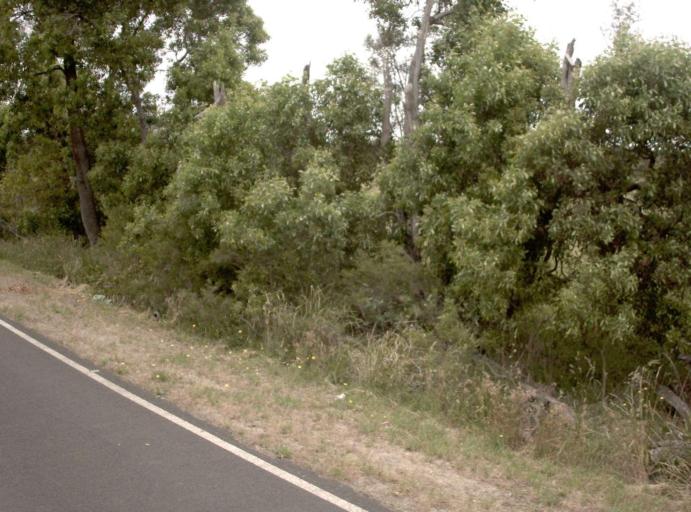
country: AU
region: Victoria
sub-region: Latrobe
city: Traralgon
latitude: -38.4844
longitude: 146.8204
